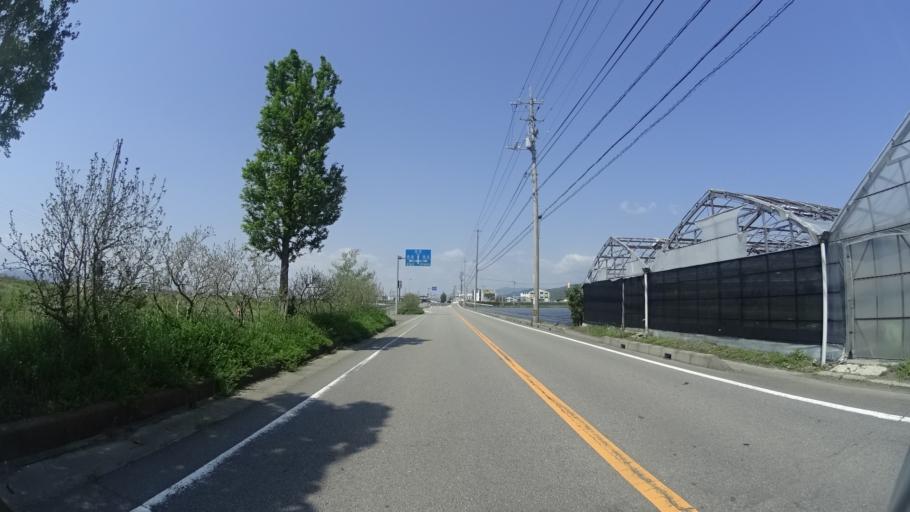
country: JP
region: Tokushima
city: Narutocho-mitsuishi
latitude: 34.1601
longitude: 134.5836
